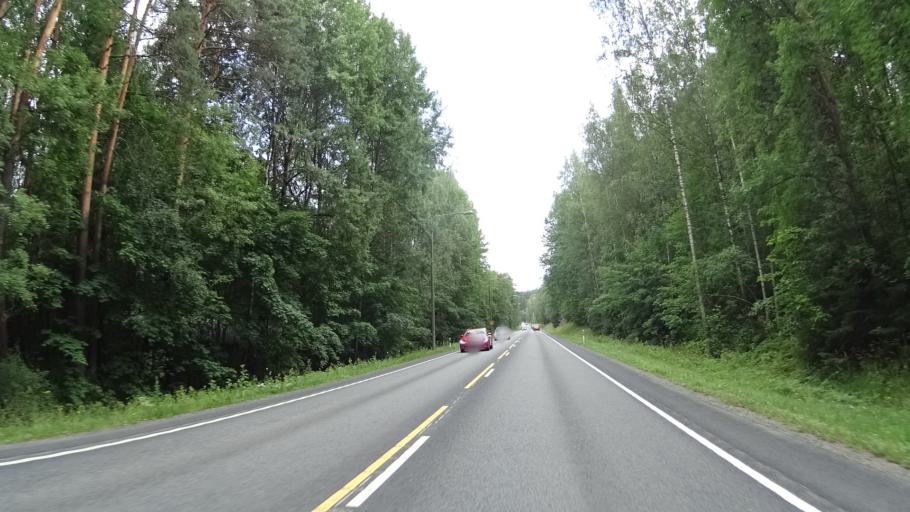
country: FI
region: Pirkanmaa
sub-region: Tampere
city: Kangasala
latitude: 61.4246
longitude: 24.1369
